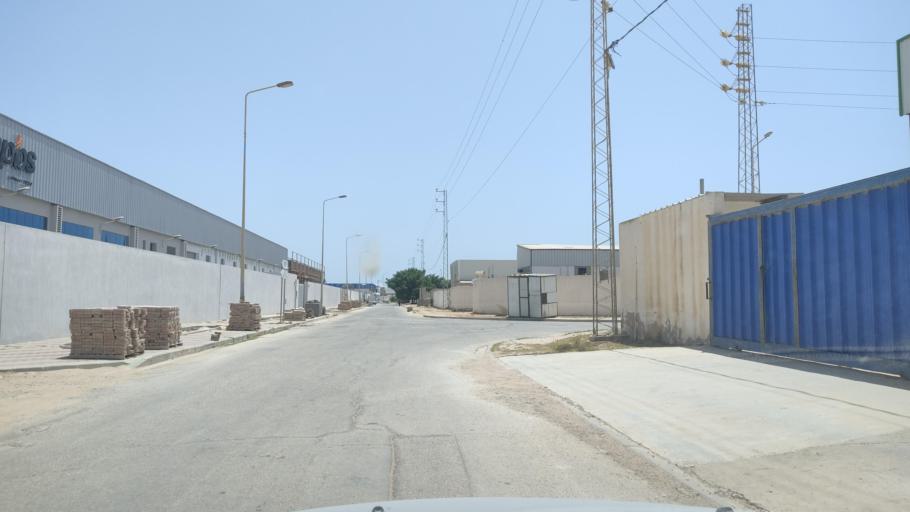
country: TN
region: Safaqis
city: Sfax
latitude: 34.6646
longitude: 10.6986
